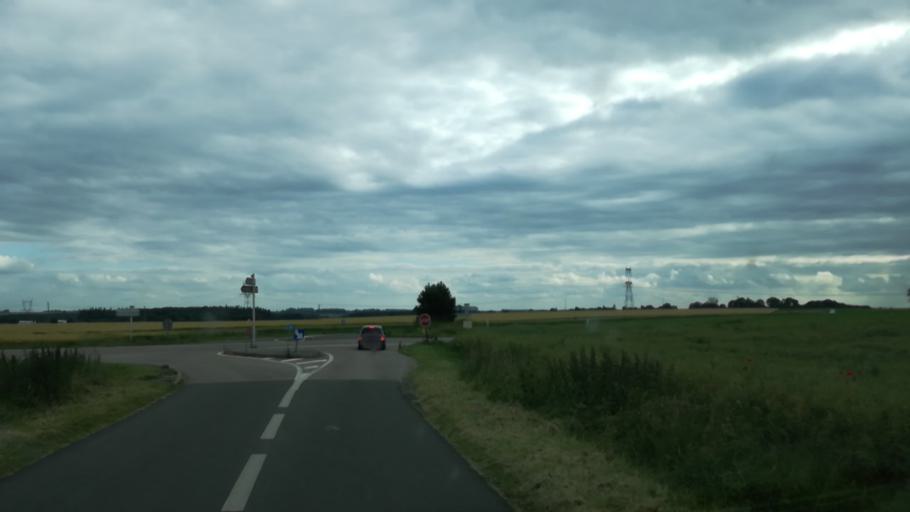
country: FR
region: Haute-Normandie
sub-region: Departement de l'Eure
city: Bourg-Achard
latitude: 49.3034
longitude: 0.7937
